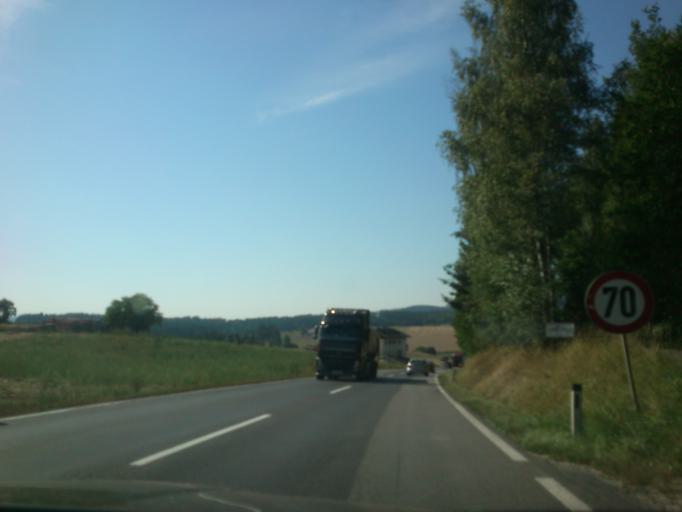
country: AT
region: Upper Austria
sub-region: Politischer Bezirk Freistadt
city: Freistadt
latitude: 48.4665
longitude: 14.5023
